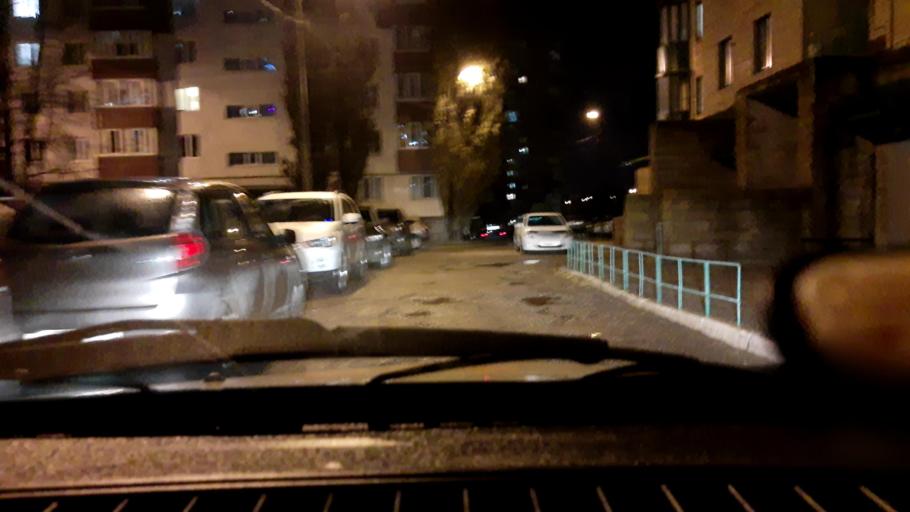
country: RU
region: Bashkortostan
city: Ufa
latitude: 54.7640
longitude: 56.0233
